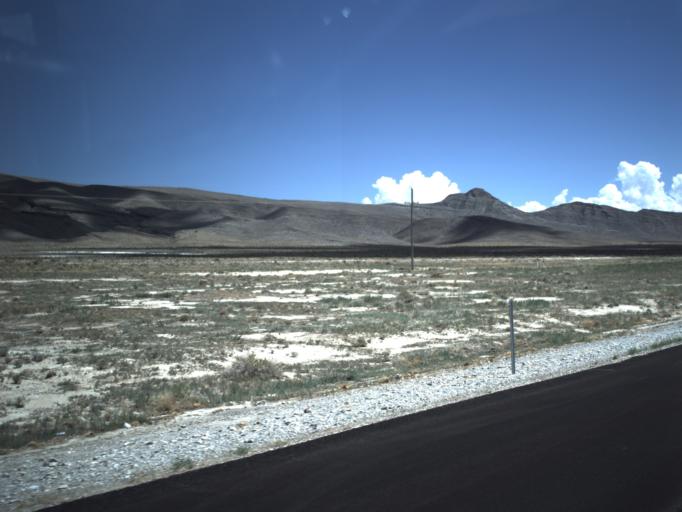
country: US
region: Utah
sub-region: Beaver County
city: Milford
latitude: 39.0511
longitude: -113.4206
